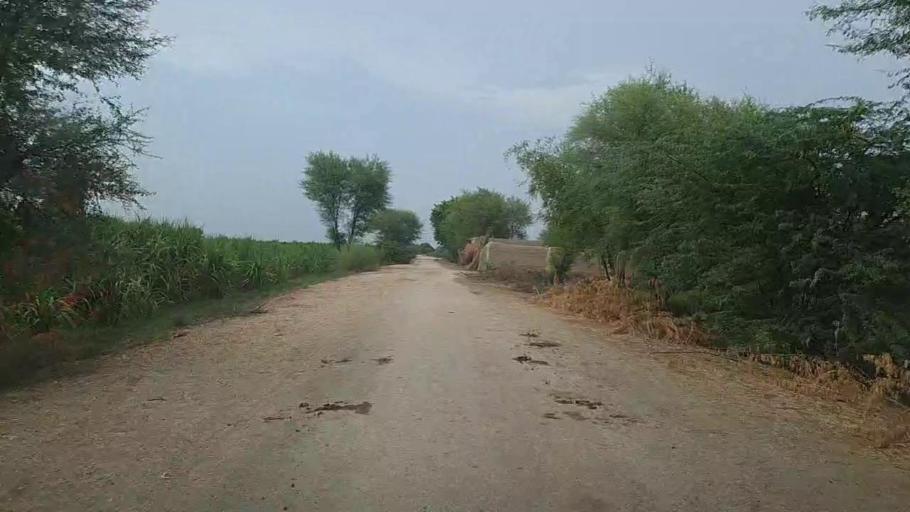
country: PK
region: Sindh
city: Karaundi
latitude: 26.9779
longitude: 68.4339
